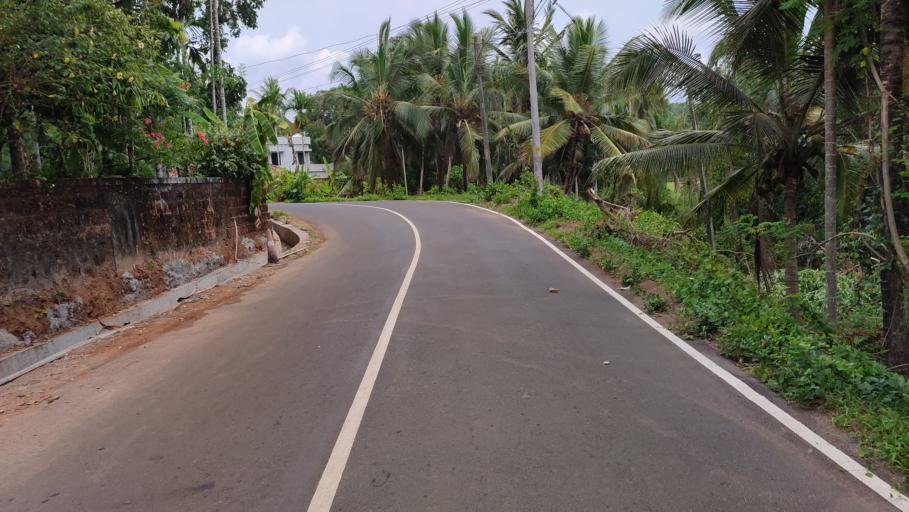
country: IN
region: Kerala
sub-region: Kasaragod District
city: Kannangad
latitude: 12.3200
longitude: 75.1135
